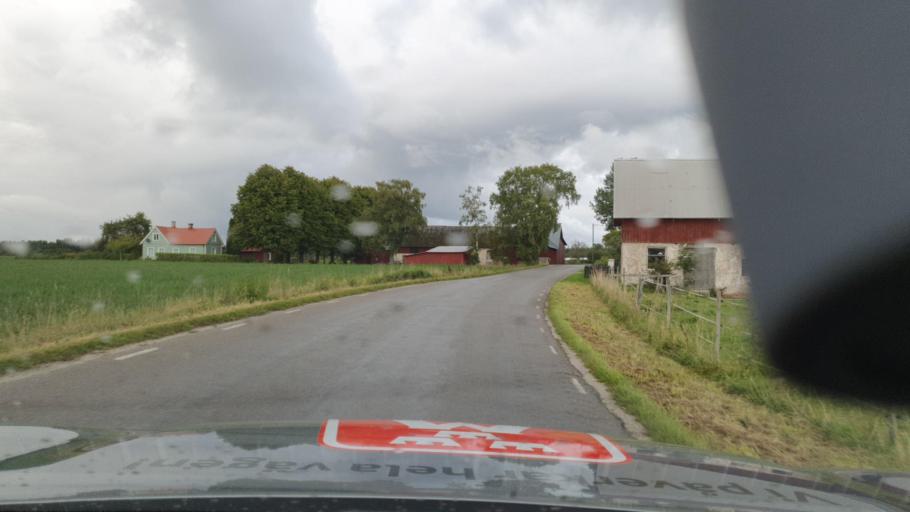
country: SE
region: Gotland
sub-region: Gotland
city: Vibble
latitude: 57.5033
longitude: 18.2021
